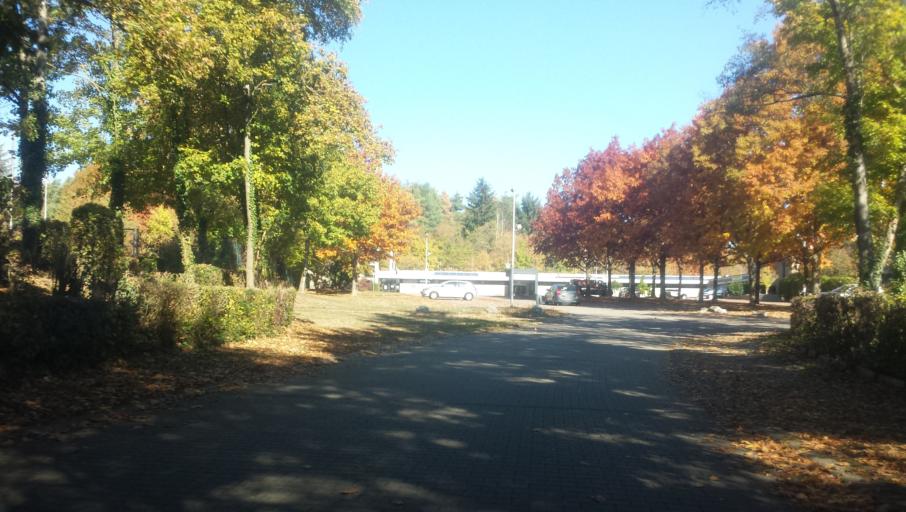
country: DE
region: Hesse
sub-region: Regierungsbezirk Darmstadt
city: Rossdorf
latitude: 49.8682
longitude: 8.7610
